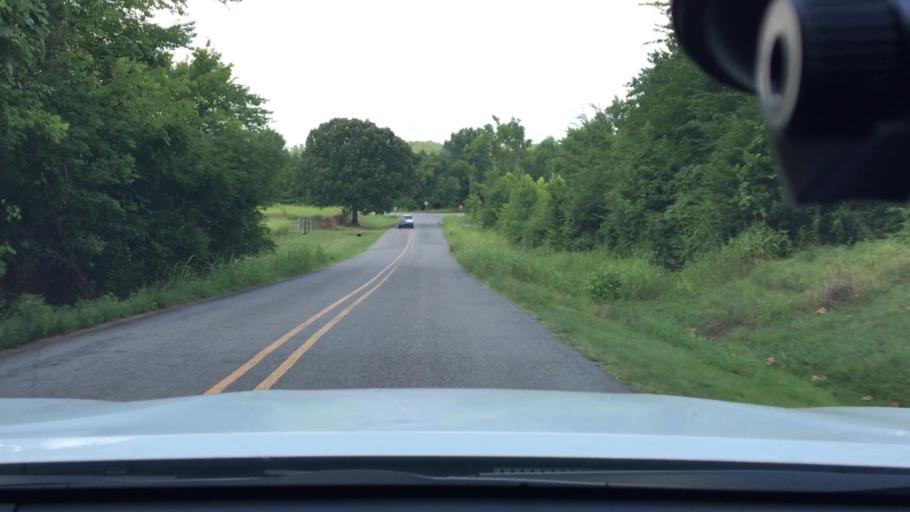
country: US
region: Arkansas
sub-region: Logan County
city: Paris
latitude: 35.2683
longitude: -93.6812
